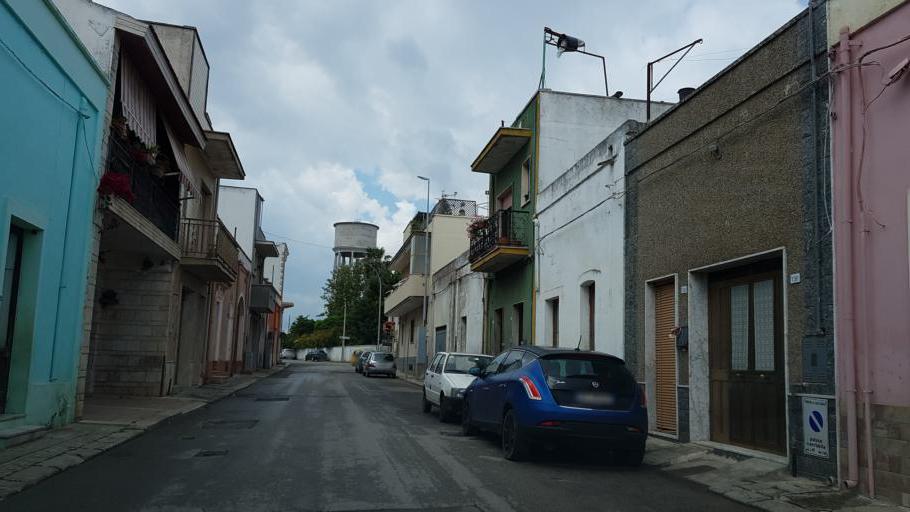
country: IT
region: Apulia
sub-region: Provincia di Brindisi
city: San Donaci
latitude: 40.4501
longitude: 17.9199
